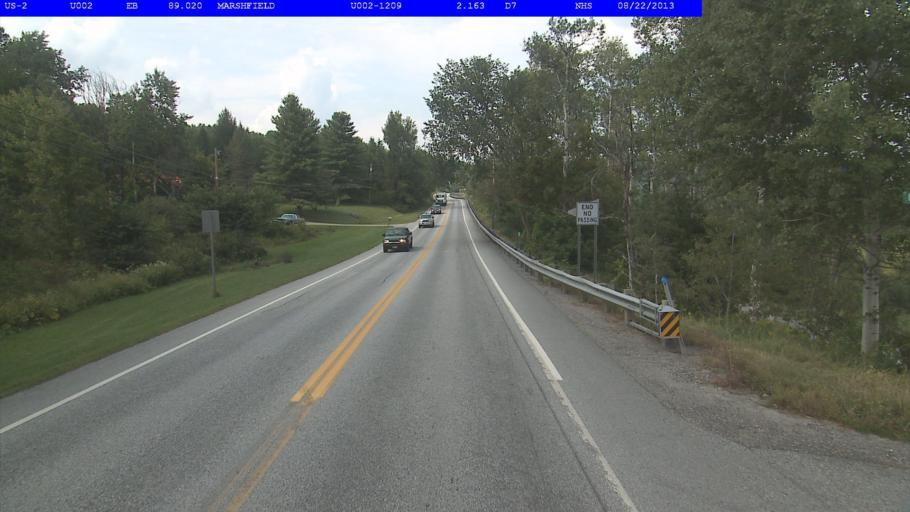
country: US
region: Vermont
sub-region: Washington County
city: Barre
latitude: 44.3020
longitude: -72.3986
